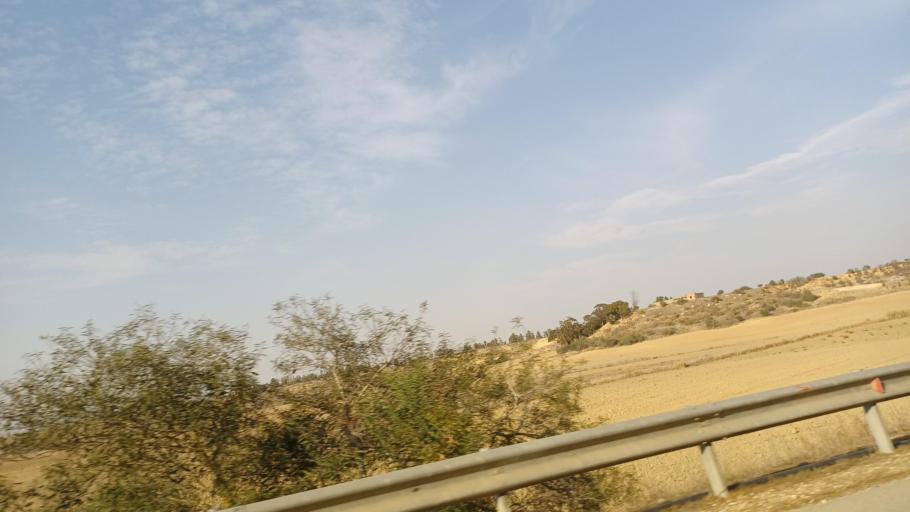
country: CY
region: Ammochostos
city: Avgorou
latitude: 35.0664
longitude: 33.8515
